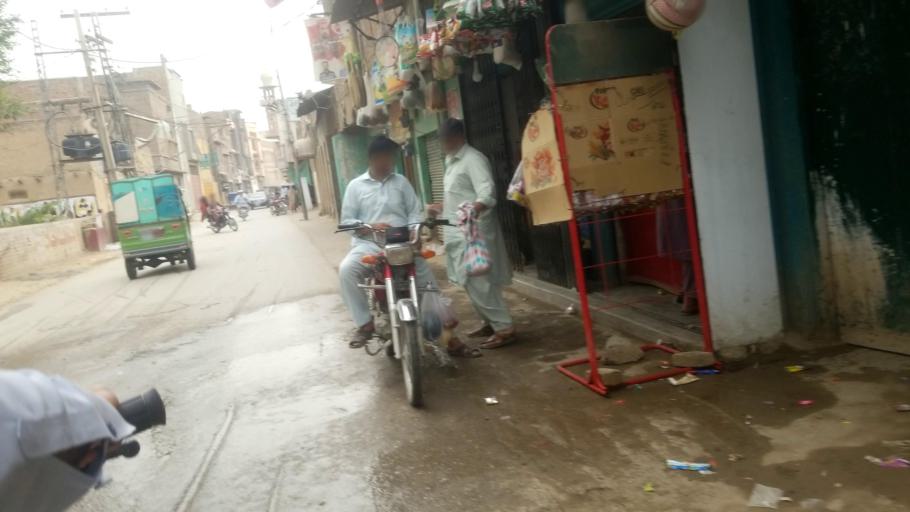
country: PK
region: Khyber Pakhtunkhwa
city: Peshawar
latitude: 33.9924
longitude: 71.5557
